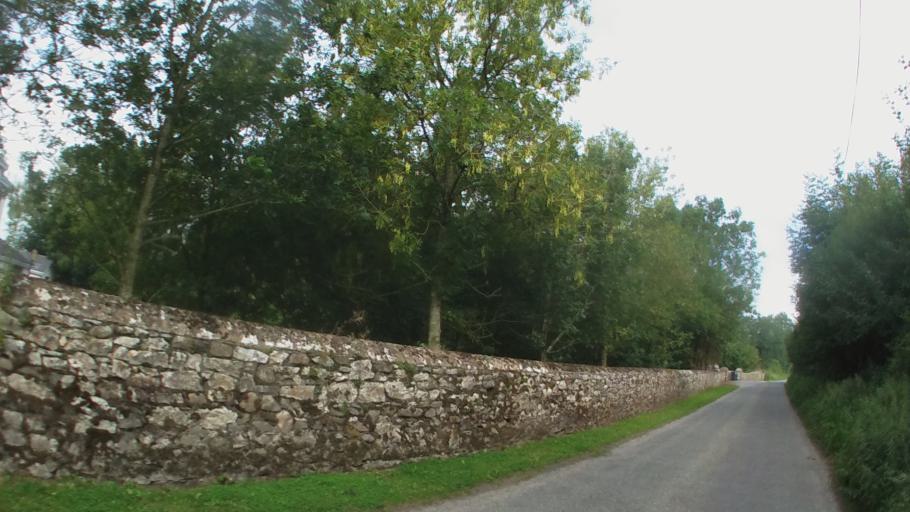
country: IE
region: Leinster
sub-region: Kilkenny
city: Kilkenny
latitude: 52.6895
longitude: -7.1880
